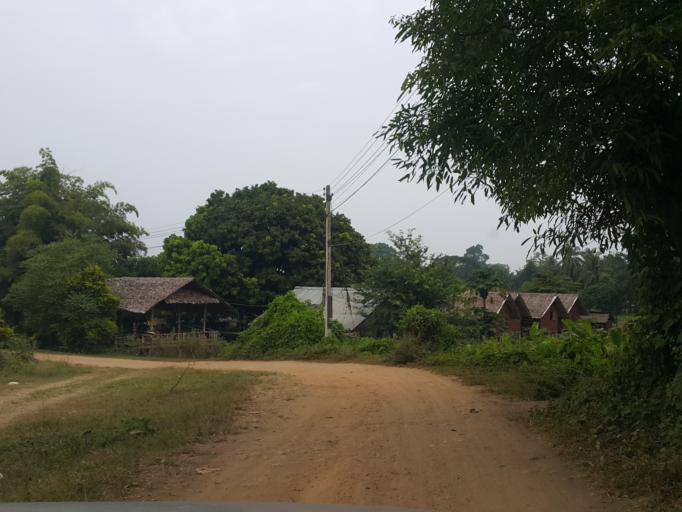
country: TH
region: Chiang Mai
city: Pai
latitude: 19.3603
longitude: 98.4481
